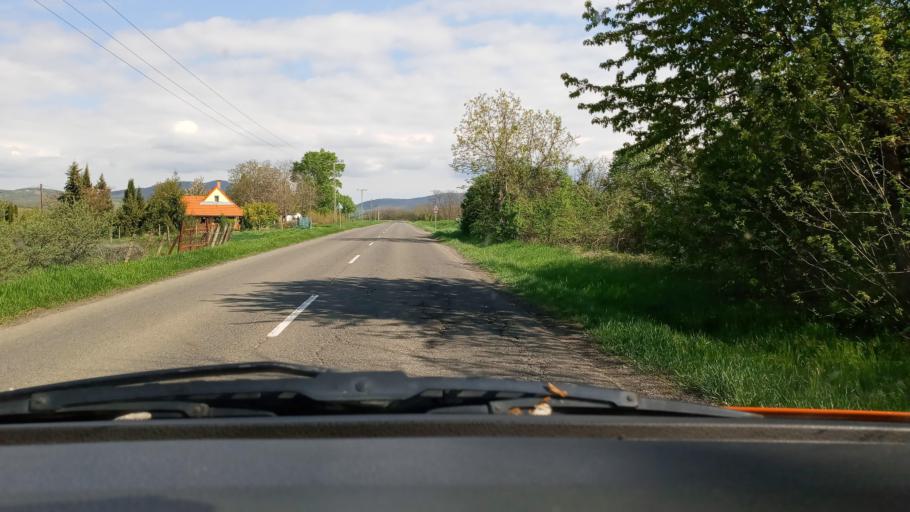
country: HU
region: Baranya
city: Hosszuheteny
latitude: 46.1181
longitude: 18.3480
